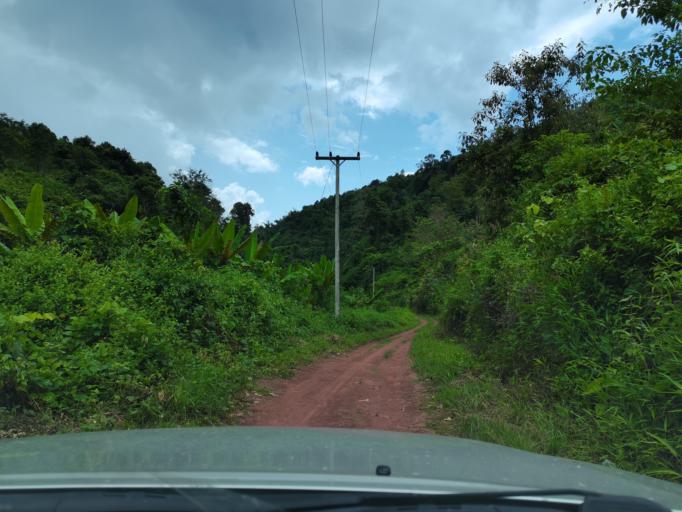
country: LA
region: Loungnamtha
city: Muang Nale
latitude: 20.5143
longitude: 101.0777
